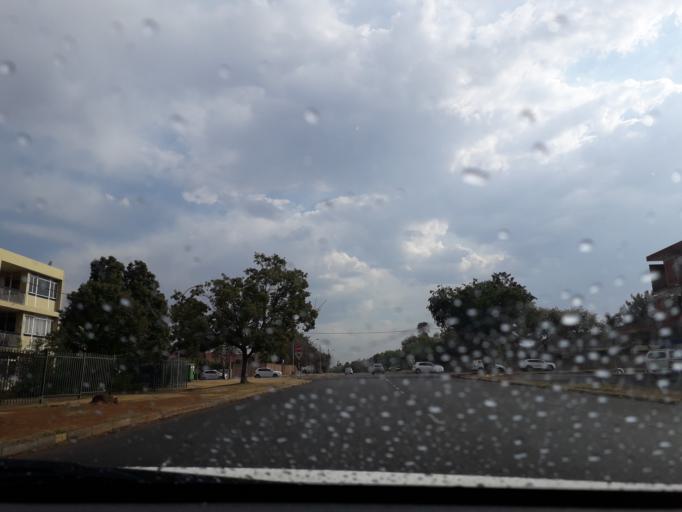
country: ZA
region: Gauteng
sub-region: City of Johannesburg Metropolitan Municipality
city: Modderfontein
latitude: -26.0927
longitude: 28.2433
